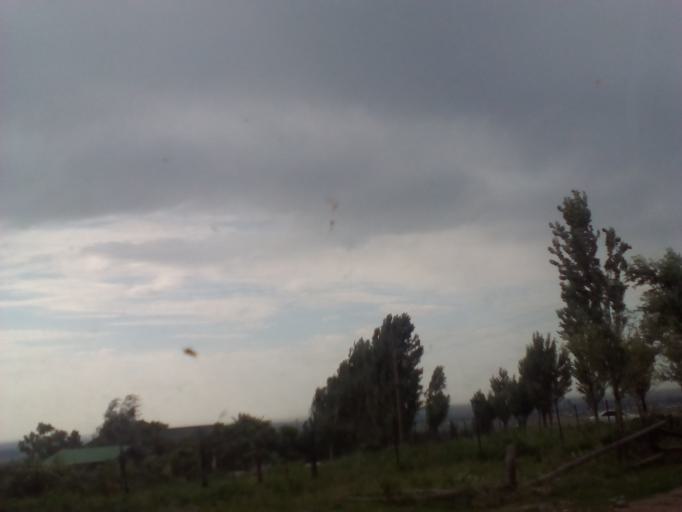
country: KZ
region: Almaty Oblysy
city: Burunday
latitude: 43.1496
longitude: 76.3855
